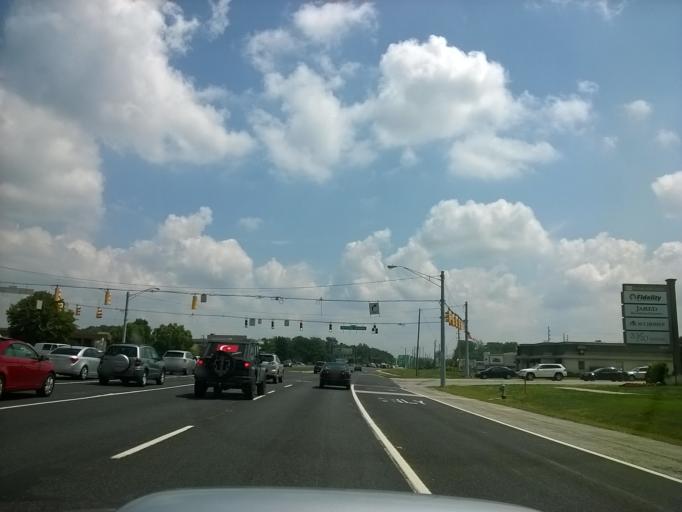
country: US
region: Indiana
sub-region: Marion County
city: Meridian Hills
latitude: 39.9120
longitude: -86.1107
